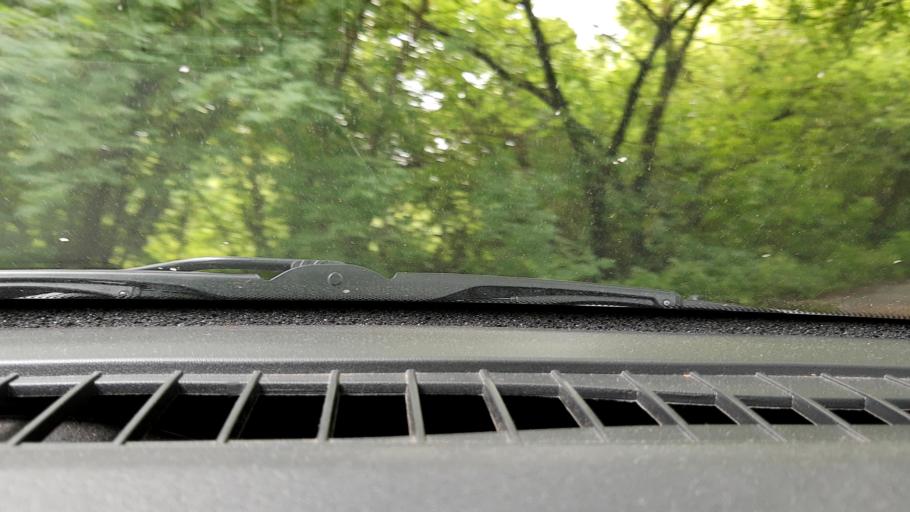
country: RU
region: Nizjnij Novgorod
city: Neklyudovo
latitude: 56.3969
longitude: 43.8501
